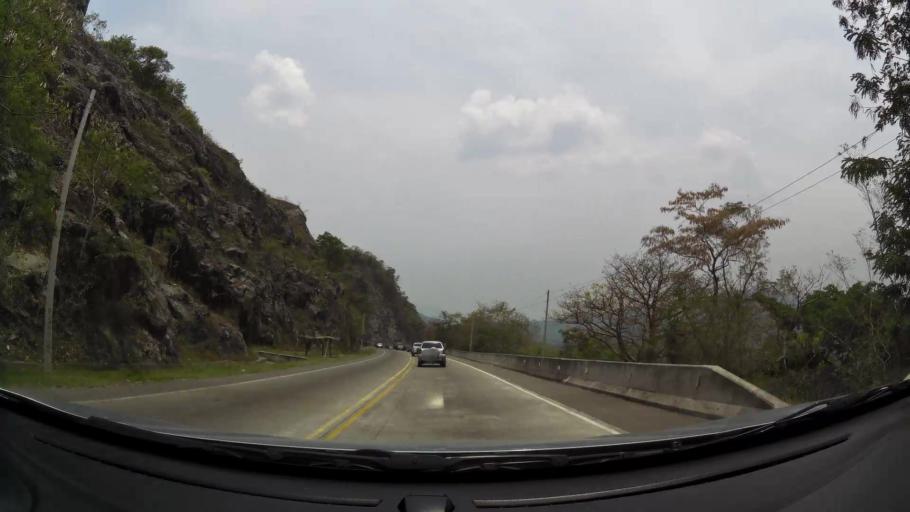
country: HN
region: Comayagua
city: Taulabe
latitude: 14.6952
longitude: -87.9524
